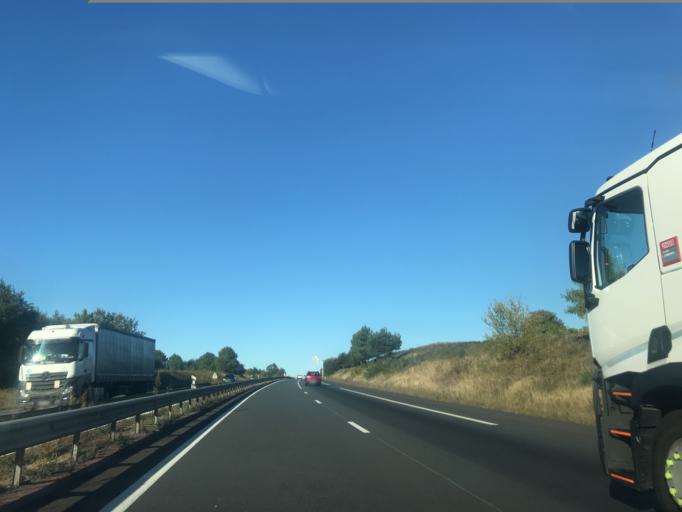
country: FR
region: Poitou-Charentes
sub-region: Departement de la Charente-Maritime
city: Montlieu-la-Garde
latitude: 45.2381
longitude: -0.2754
